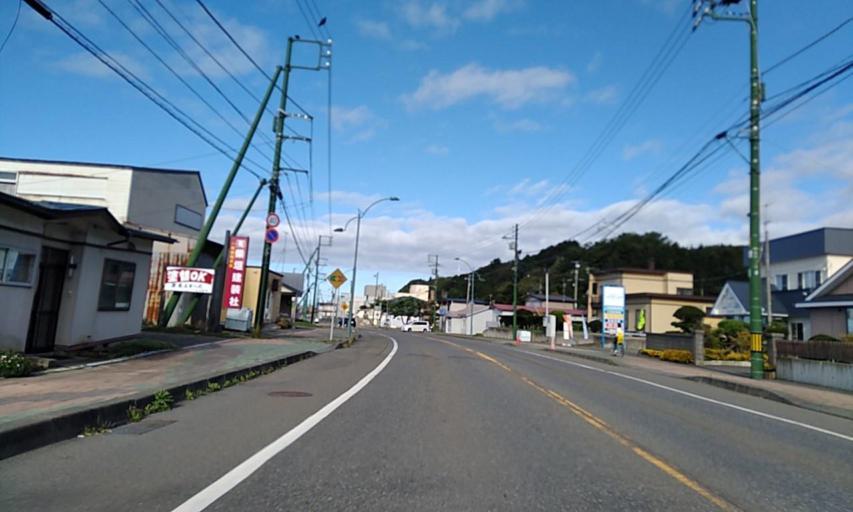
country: JP
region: Hokkaido
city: Shizunai-furukawacho
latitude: 42.2476
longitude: 142.5648
